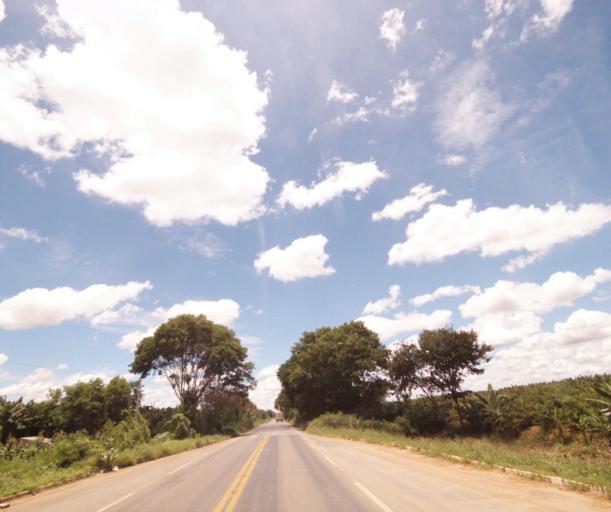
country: BR
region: Bahia
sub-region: Bom Jesus Da Lapa
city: Bom Jesus da Lapa
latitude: -13.2649
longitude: -43.5809
